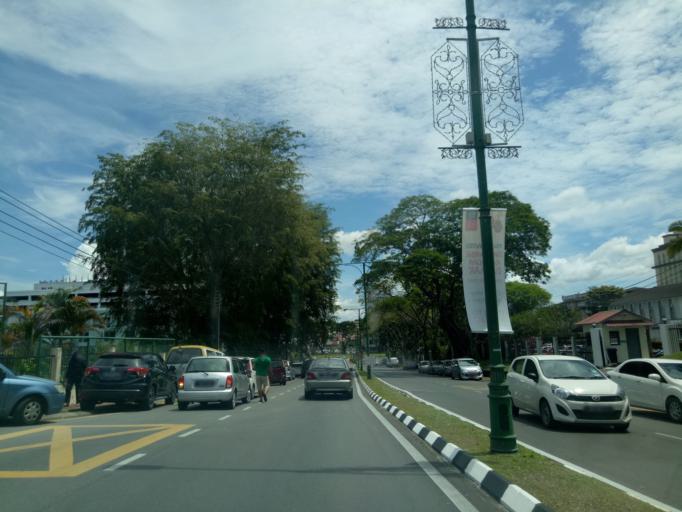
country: MY
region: Sarawak
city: Kuching
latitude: 1.5559
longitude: 110.3458
